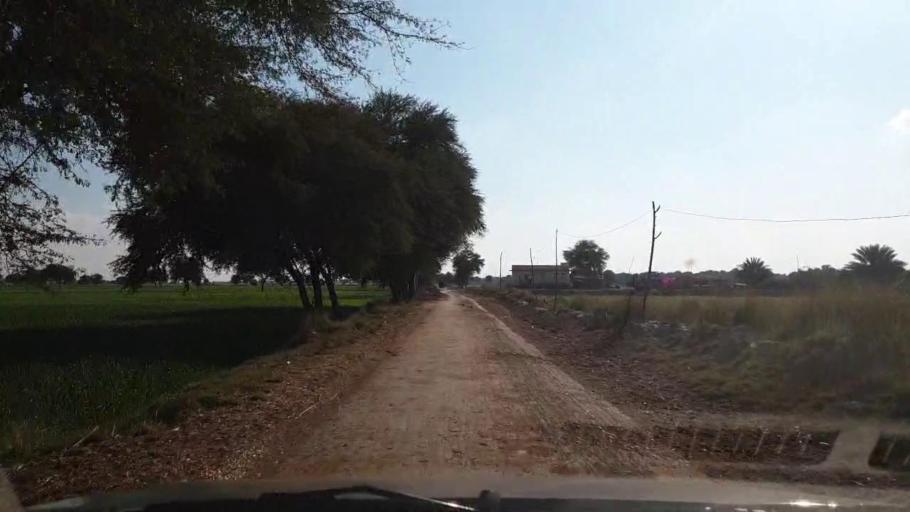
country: PK
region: Sindh
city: Sinjhoro
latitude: 25.9865
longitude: 68.7263
